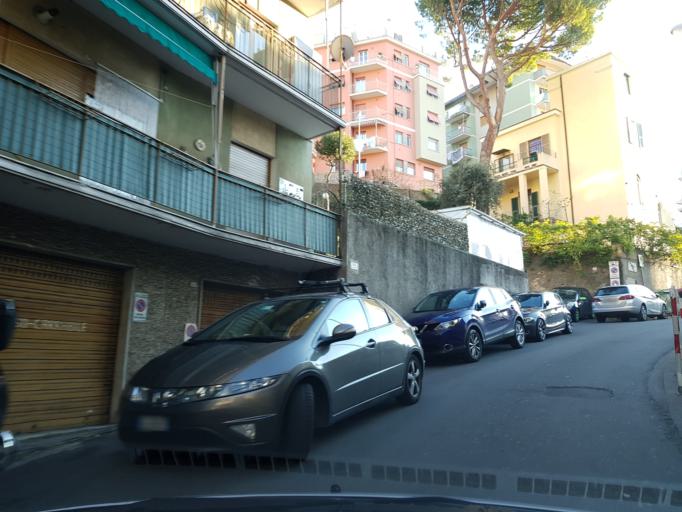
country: IT
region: Liguria
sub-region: Provincia di Genova
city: Genoa
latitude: 44.4081
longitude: 8.9816
